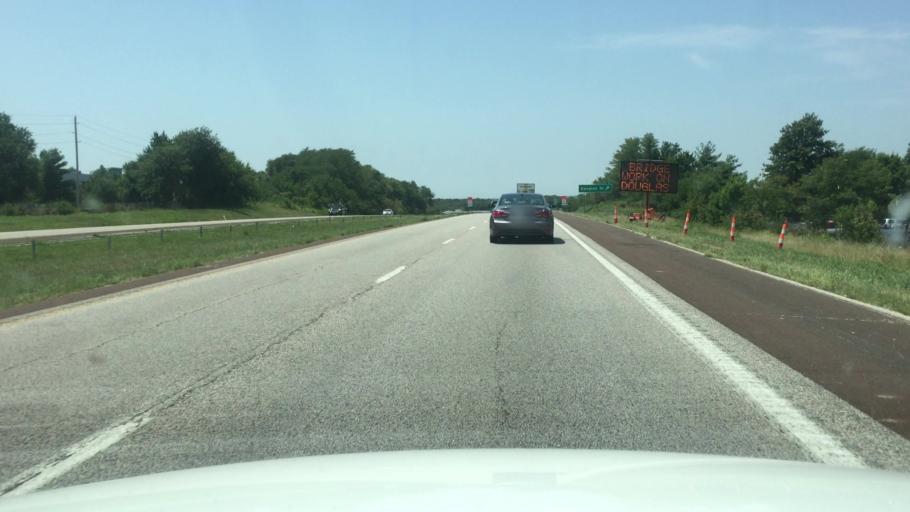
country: US
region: Missouri
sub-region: Jackson County
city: Lees Summit
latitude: 38.9450
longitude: -94.3696
